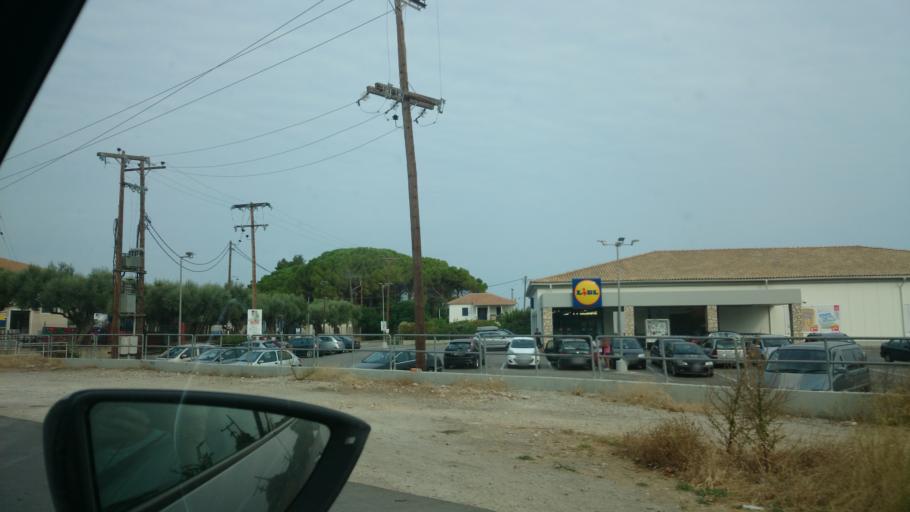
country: GR
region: Ionian Islands
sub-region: Lefkada
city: Lefkada
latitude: 38.8159
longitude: 20.7117
